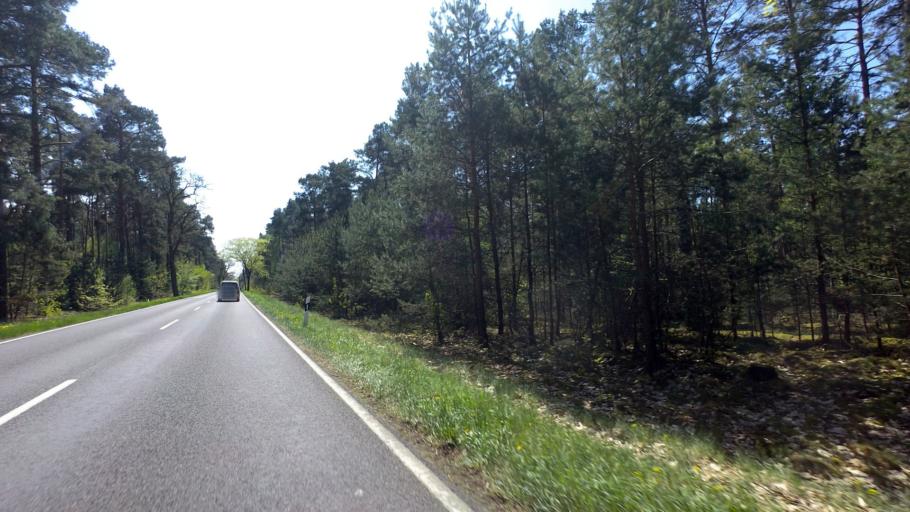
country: DE
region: Brandenburg
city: Halbe
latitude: 52.1260
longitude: 13.7551
